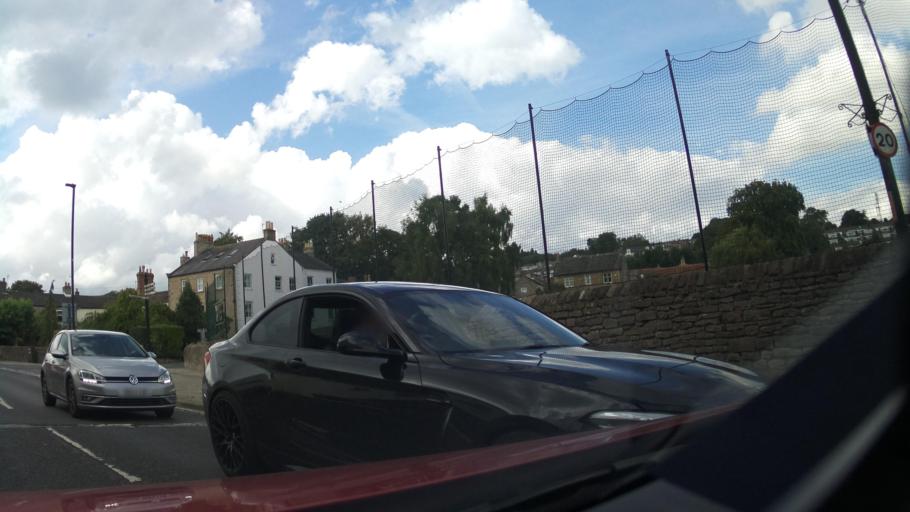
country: GB
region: England
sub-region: North Yorkshire
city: Catterick Garrison
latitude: 54.4046
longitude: -1.7408
